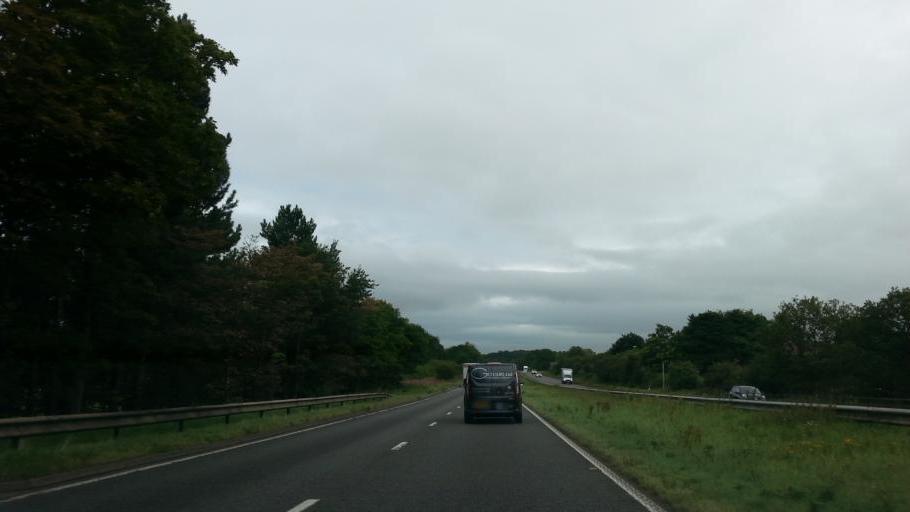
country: GB
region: England
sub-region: Nottinghamshire
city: Babworth
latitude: 53.3214
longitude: -1.0277
